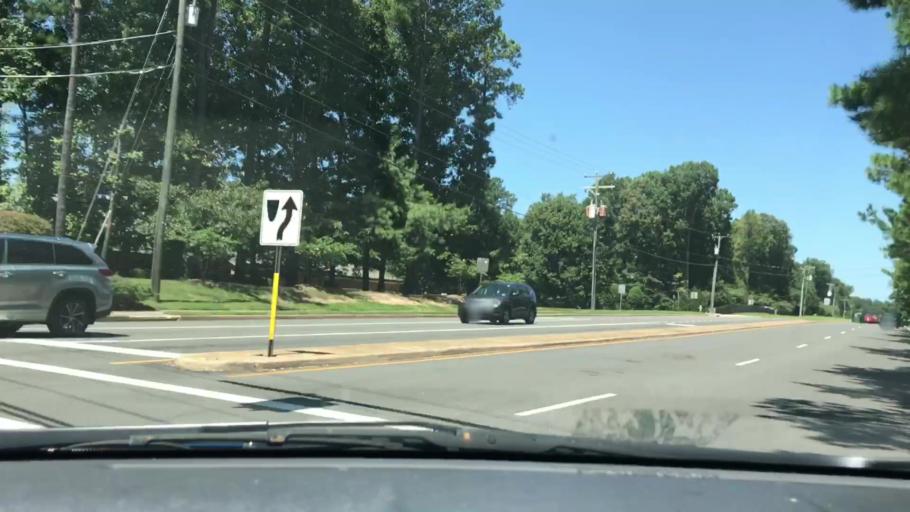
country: US
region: Virginia
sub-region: Henrico County
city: Short Pump
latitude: 37.6075
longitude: -77.6066
